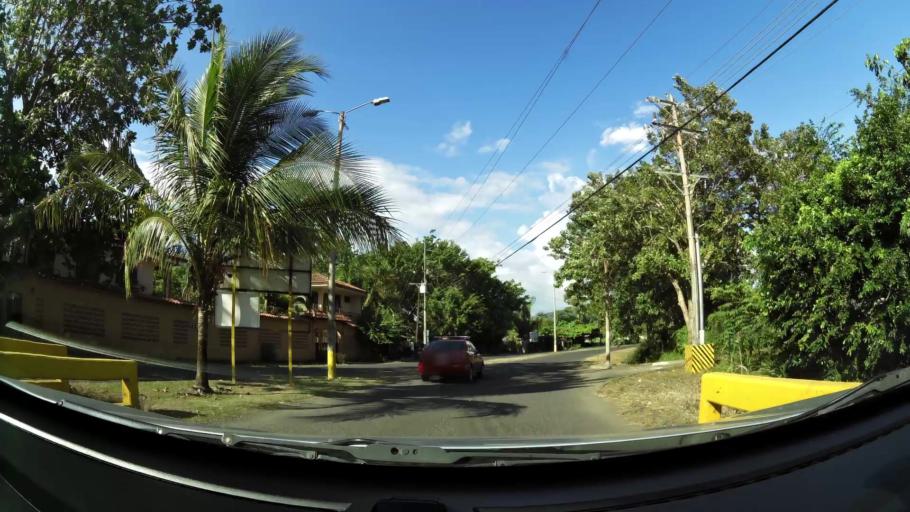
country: CR
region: Puntarenas
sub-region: Canton de Garabito
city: Jaco
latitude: 9.6227
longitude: -84.6371
